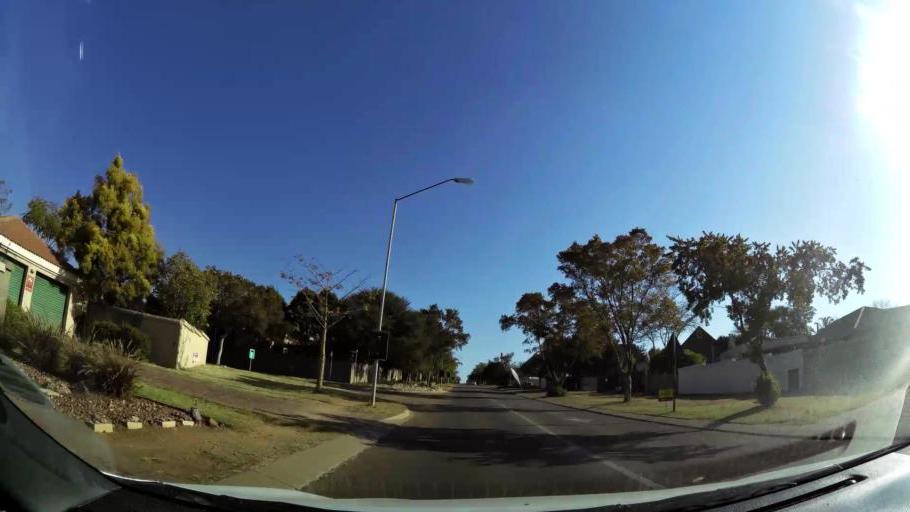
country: ZA
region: Gauteng
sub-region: City of Tshwane Metropolitan Municipality
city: Centurion
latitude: -25.8356
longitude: 28.2971
